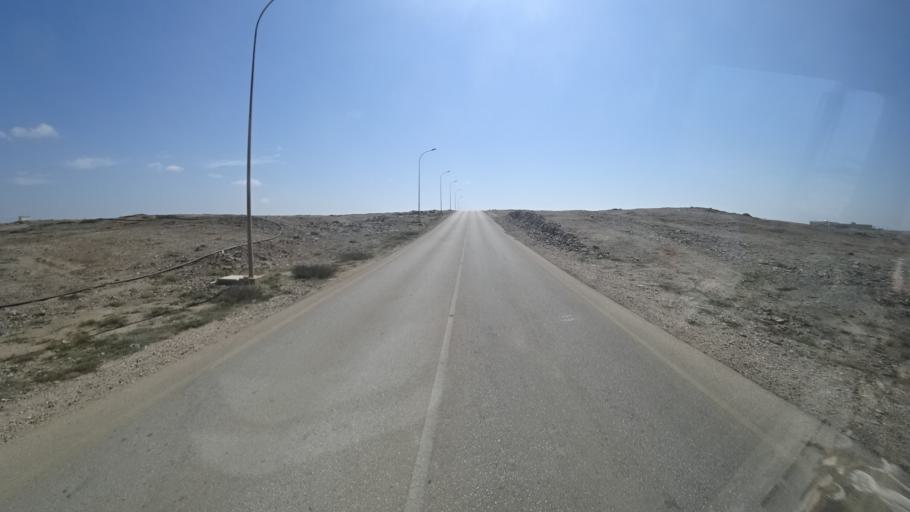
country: OM
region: Zufar
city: Salalah
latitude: 16.9681
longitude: 54.7316
